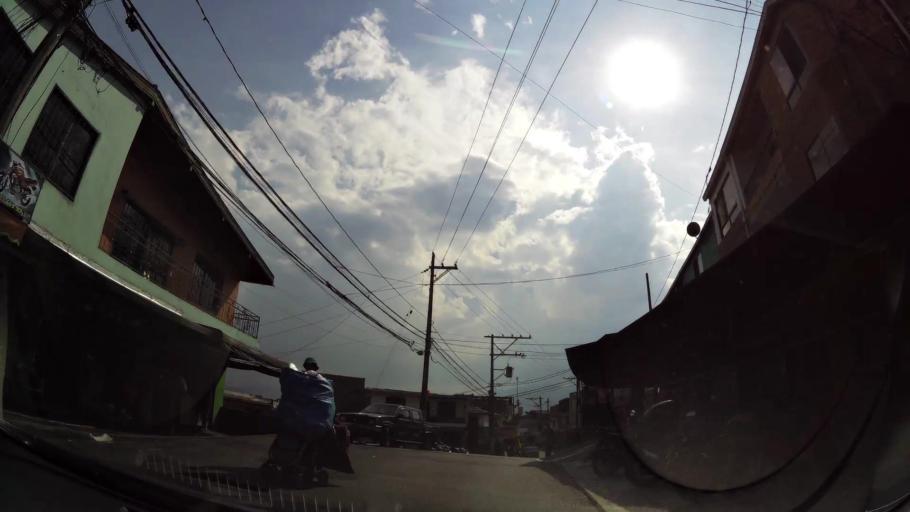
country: CO
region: Antioquia
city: Medellin
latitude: 6.2870
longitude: -75.5928
